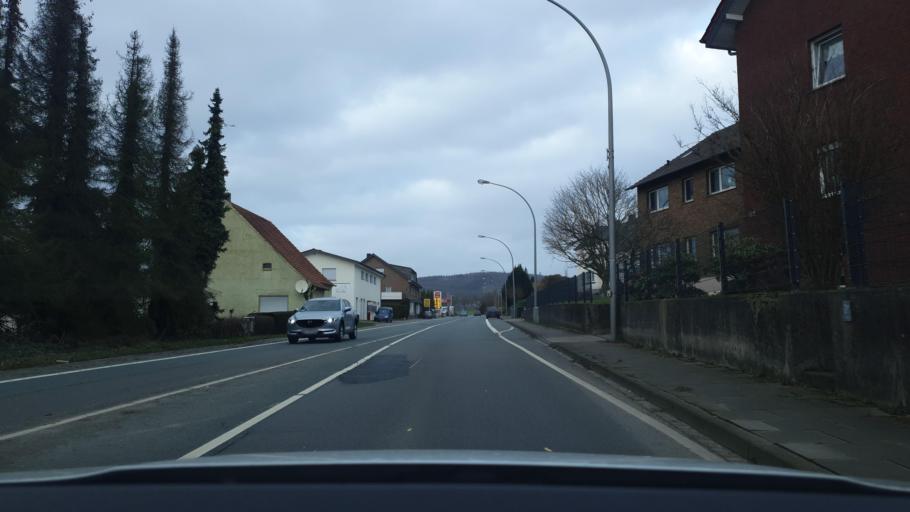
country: DE
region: North Rhine-Westphalia
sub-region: Regierungsbezirk Detmold
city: Huellhorst
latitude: 52.2675
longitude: 8.6355
